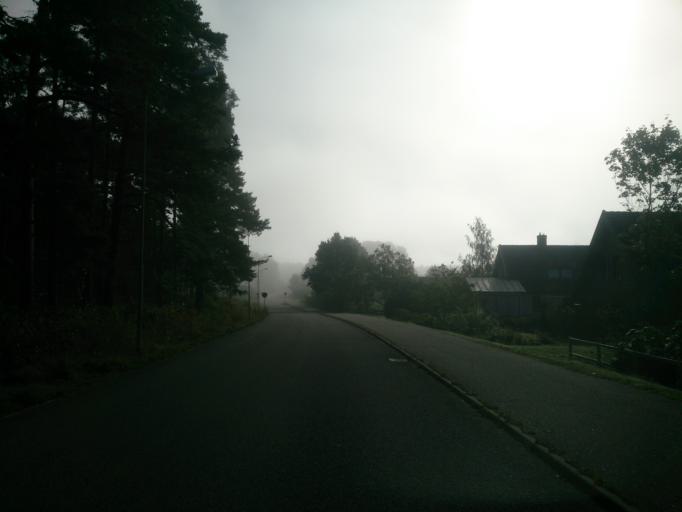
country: SE
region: OEstergoetland
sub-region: Linkopings Kommun
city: Sturefors
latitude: 58.3049
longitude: 15.8732
